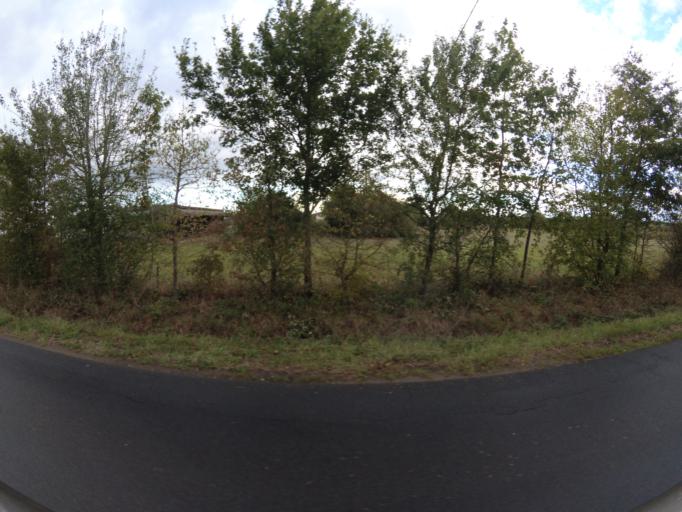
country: FR
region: Pays de la Loire
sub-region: Departement de la Loire-Atlantique
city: Saint-Lumine-de-Clisson
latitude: 47.0718
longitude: -1.3250
